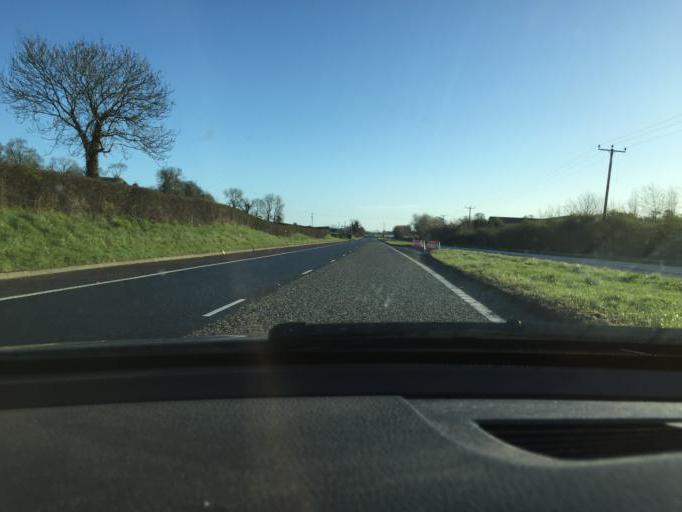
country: GB
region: Northern Ireland
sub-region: Banbridge District
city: Banbridge
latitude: 54.3622
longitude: -6.2257
